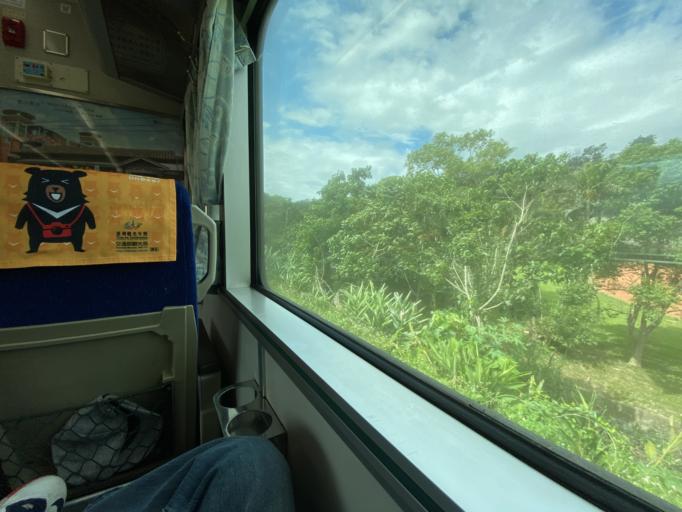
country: TW
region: Taiwan
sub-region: Taitung
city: Taitung
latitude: 22.9081
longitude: 121.1374
